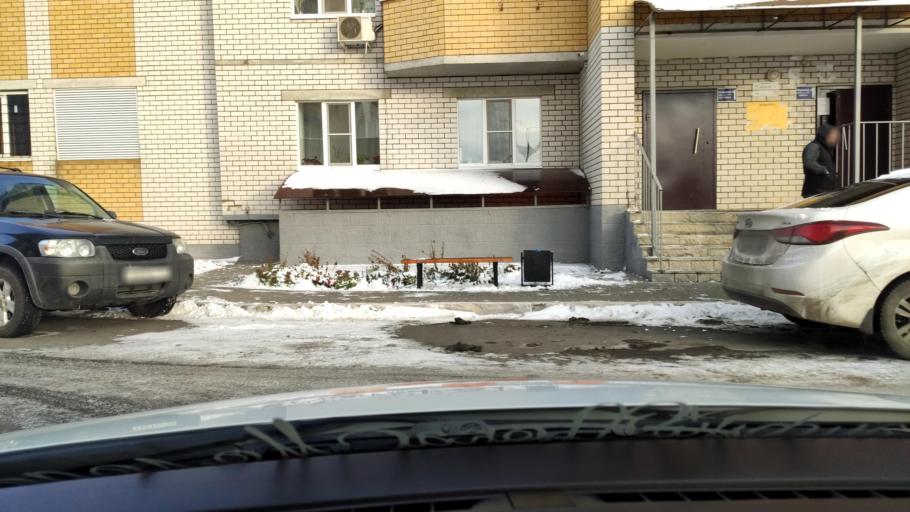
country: RU
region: Voronezj
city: Podgornoye
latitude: 51.7198
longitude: 39.1404
